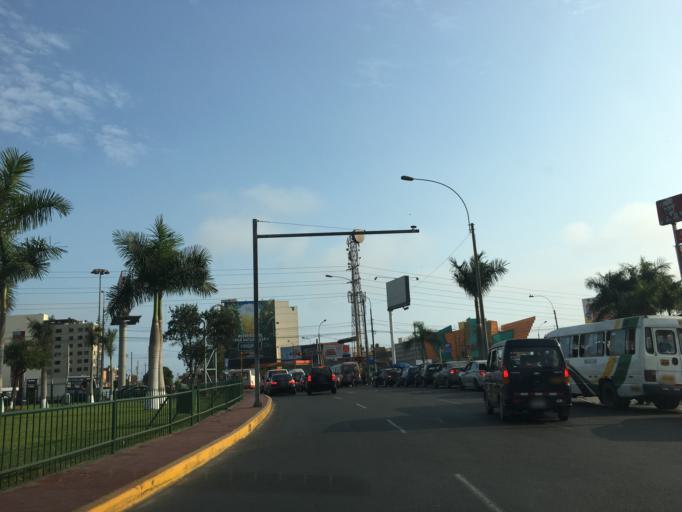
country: PE
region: Callao
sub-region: Callao
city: Callao
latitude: -12.0774
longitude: -77.0814
